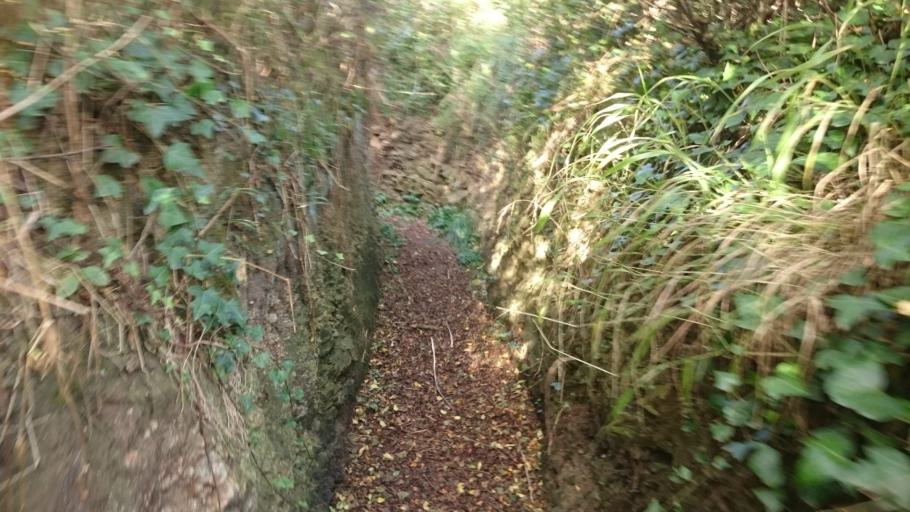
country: GG
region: St Peter Port
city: Saint Peter Port
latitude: 49.4269
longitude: -2.6672
